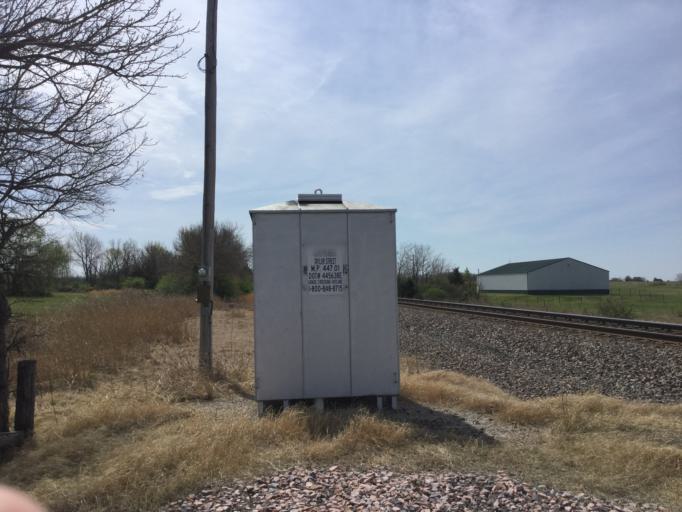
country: US
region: Kansas
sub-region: Montgomery County
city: Independence
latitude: 37.2510
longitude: -95.7351
